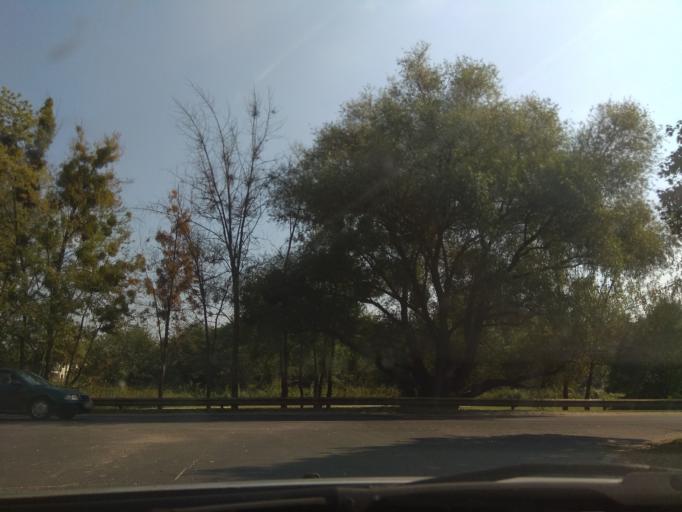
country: HU
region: Borsod-Abauj-Zemplen
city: Miskolc
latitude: 48.0751
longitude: 20.7638
